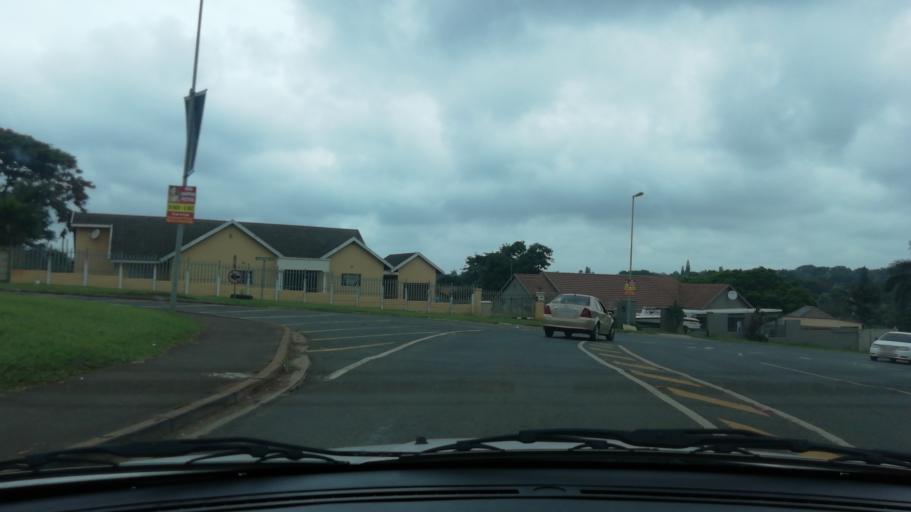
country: ZA
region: KwaZulu-Natal
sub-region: uThungulu District Municipality
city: Empangeni
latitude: -28.7592
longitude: 31.9015
